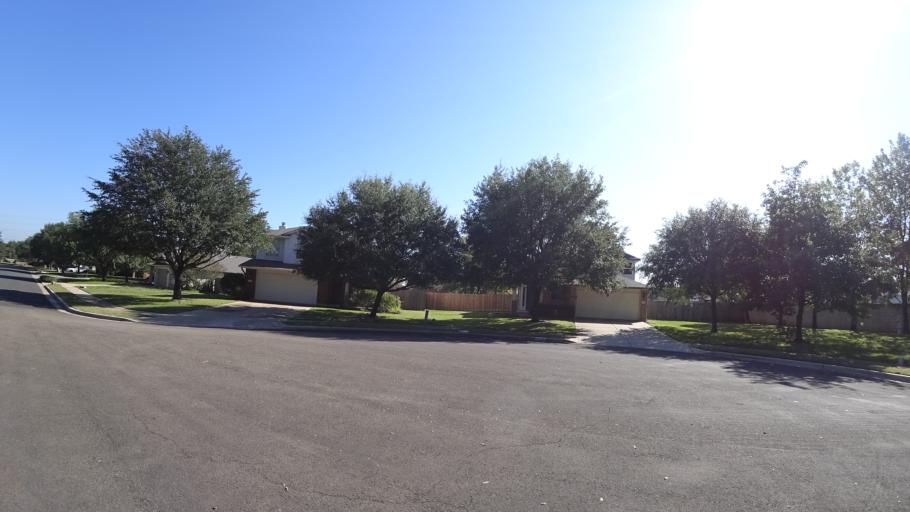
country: US
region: Texas
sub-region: Travis County
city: Shady Hollow
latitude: 30.1957
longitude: -97.8591
